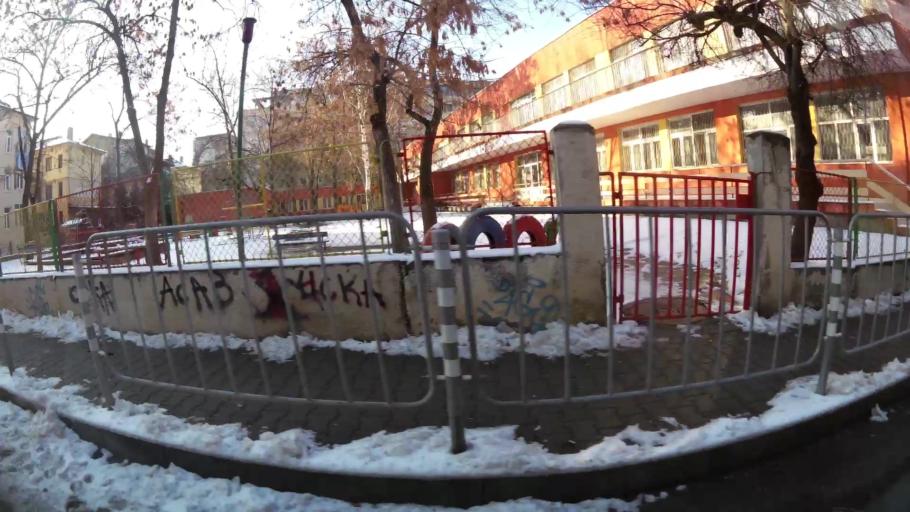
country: BG
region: Sofia-Capital
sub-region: Stolichna Obshtina
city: Sofia
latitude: 42.6777
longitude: 23.3617
